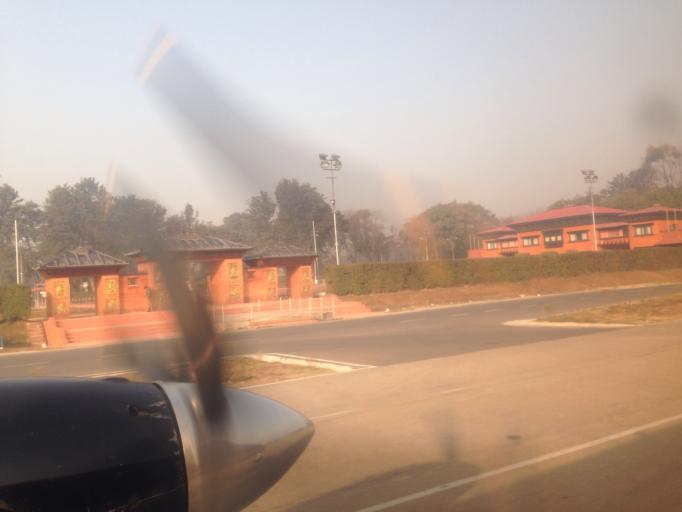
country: NP
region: Central Region
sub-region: Bagmati Zone
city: Kathmandu
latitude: 27.7052
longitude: 85.3599
